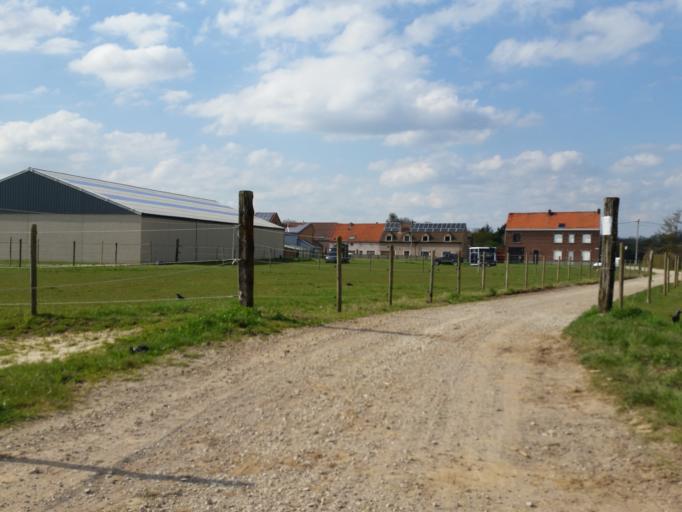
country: BE
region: Flanders
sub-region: Provincie Vlaams-Brabant
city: Kampenhout
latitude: 50.9226
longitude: 4.5573
